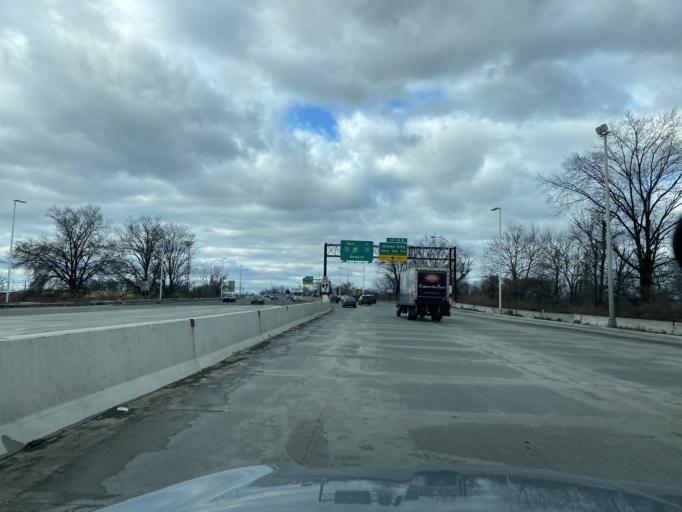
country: US
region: New Jersey
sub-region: Hudson County
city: Jersey City
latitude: 40.7072
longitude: -74.0619
